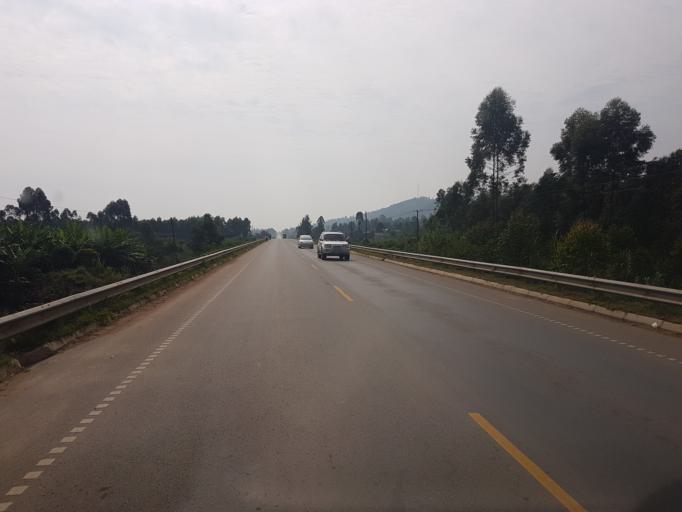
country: UG
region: Western Region
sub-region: Sheema District
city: Kibingo
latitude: -0.6442
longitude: 30.4978
